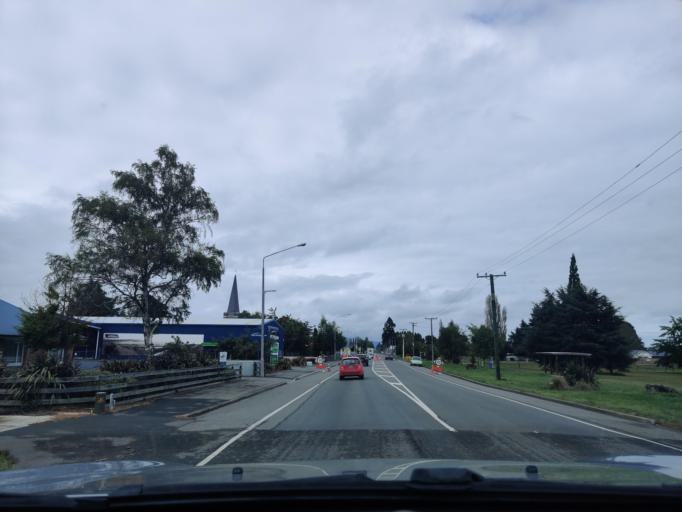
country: NZ
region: Canterbury
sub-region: Hurunui District
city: Amberley
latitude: -42.7714
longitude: 172.8503
